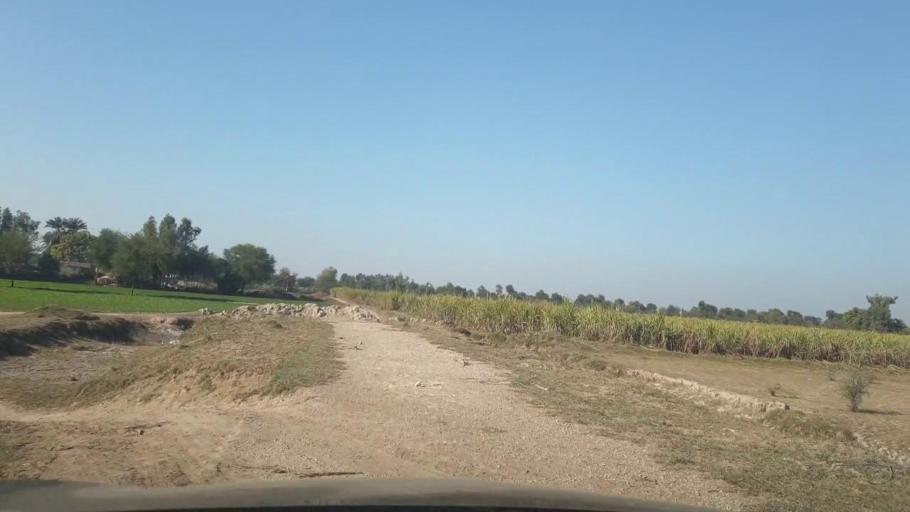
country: PK
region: Sindh
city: Mirpur Mathelo
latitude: 28.1458
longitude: 69.5916
